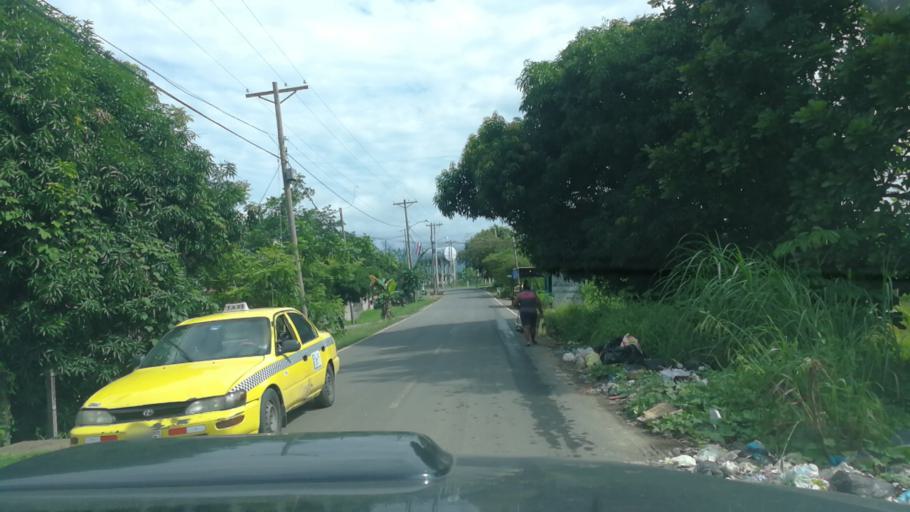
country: PA
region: Panama
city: Paso Blanco
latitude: 9.1318
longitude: -79.2540
